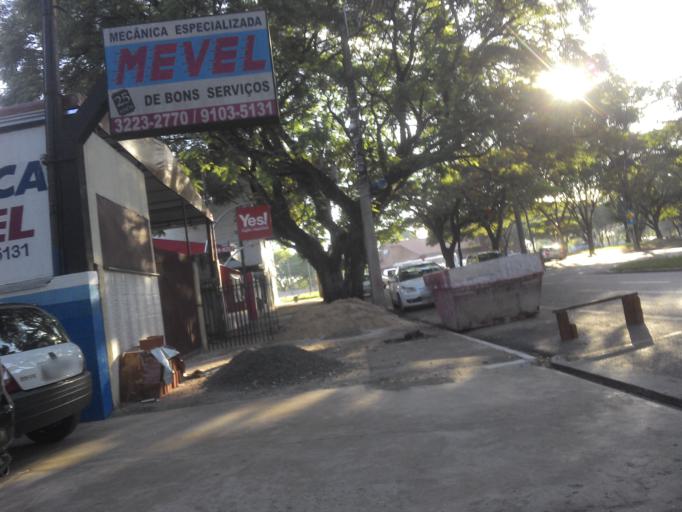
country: BR
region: Parana
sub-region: Maringa
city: Maringa
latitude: -23.4367
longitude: -51.9345
